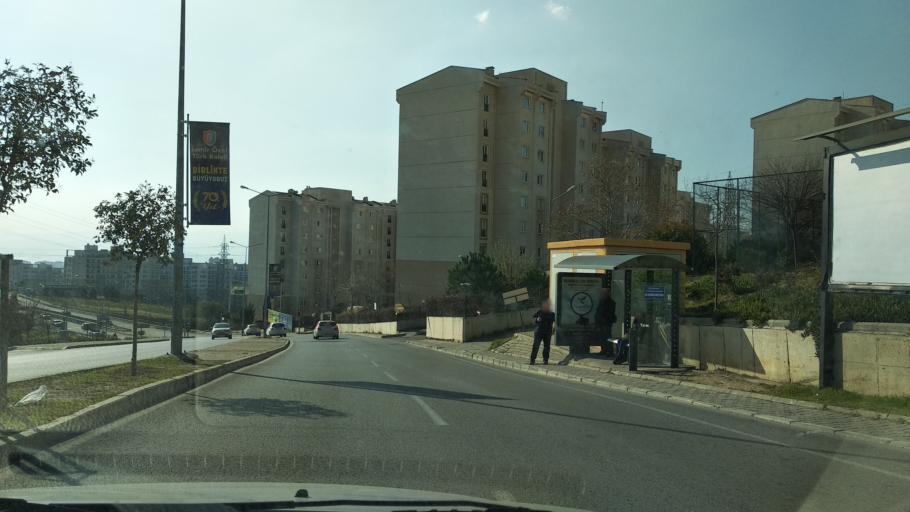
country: TR
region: Izmir
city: Karsiyaka
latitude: 38.4918
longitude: 27.0913
